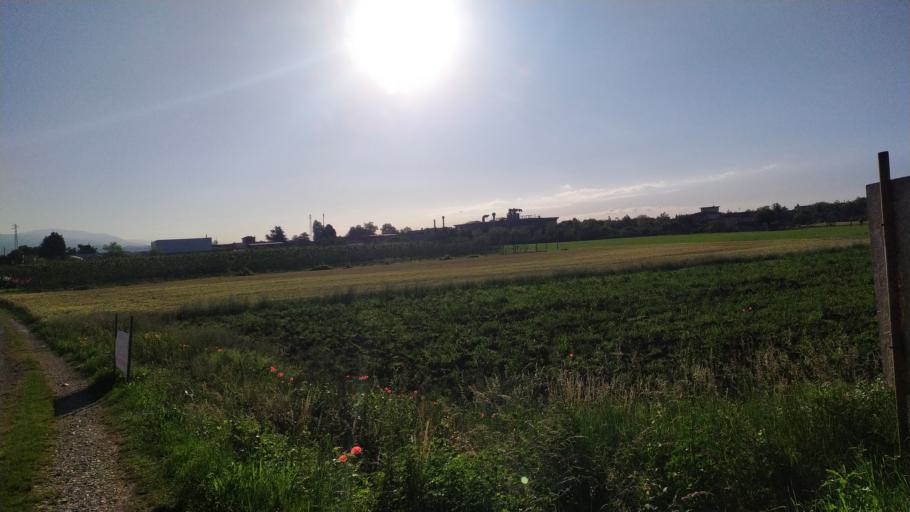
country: IT
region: Veneto
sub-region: Provincia di Vicenza
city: Malo
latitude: 45.6484
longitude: 11.4162
